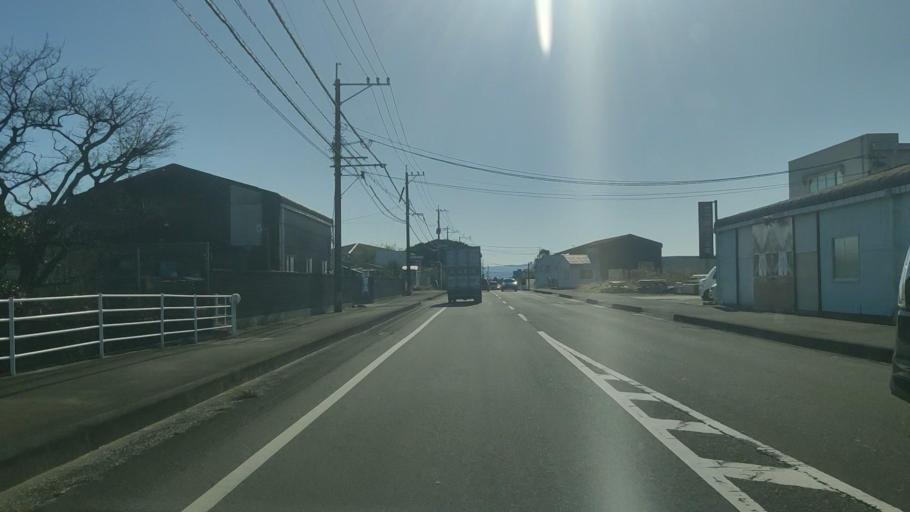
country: JP
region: Miyazaki
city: Miyazaki-shi
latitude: 31.9461
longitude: 131.4590
